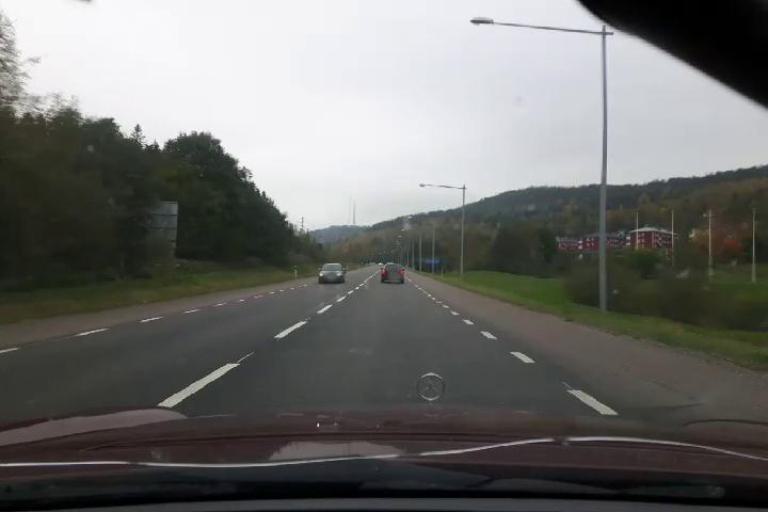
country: SE
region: Vaesternorrland
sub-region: OErnskoeldsviks Kommun
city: Ornskoldsvik
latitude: 63.2943
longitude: 18.6947
